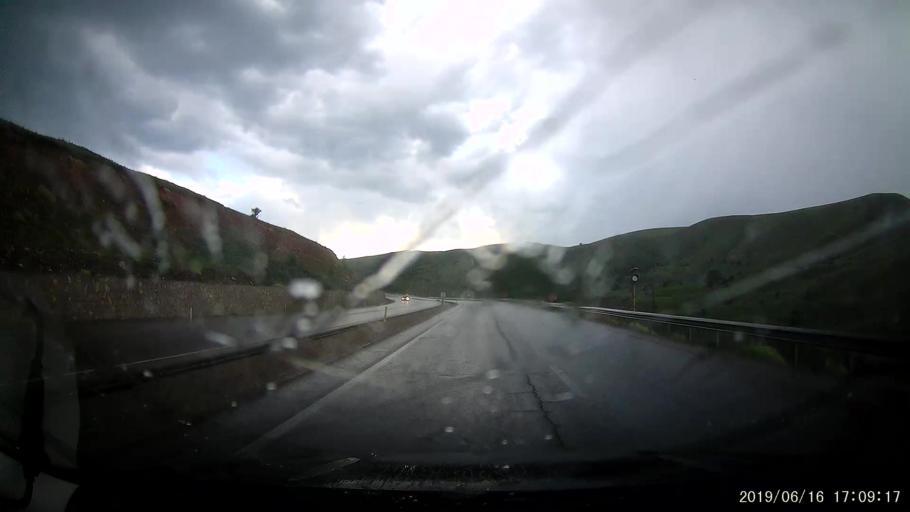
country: TR
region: Erzurum
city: Askale
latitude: 39.8974
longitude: 40.6511
